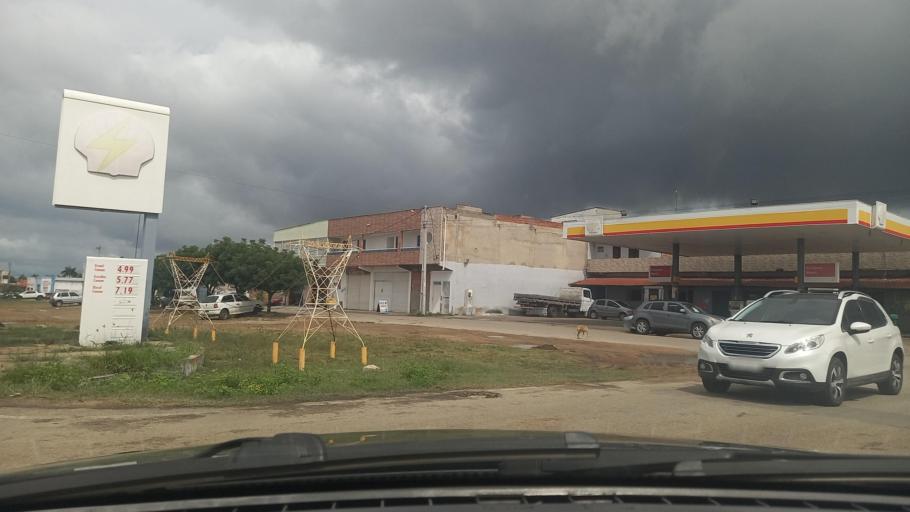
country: BR
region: Bahia
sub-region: Paulo Afonso
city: Paulo Afonso
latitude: -9.3986
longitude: -38.2431
